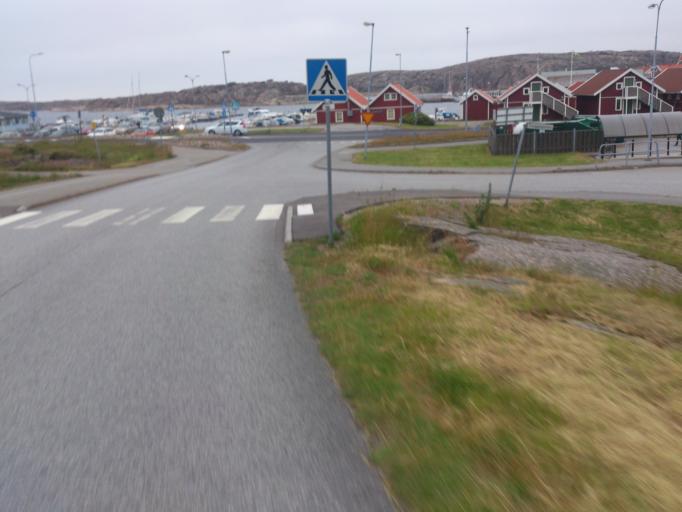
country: SE
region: Vaestra Goetaland
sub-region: Sotenas Kommun
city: Kungshamn
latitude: 58.3792
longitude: 11.2634
